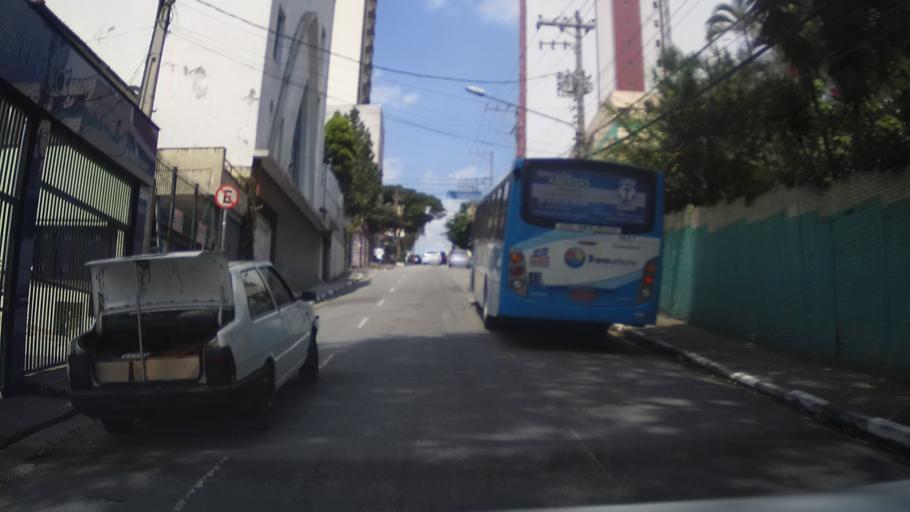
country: BR
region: Sao Paulo
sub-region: Guarulhos
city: Guarulhos
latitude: -23.4700
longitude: -46.5335
